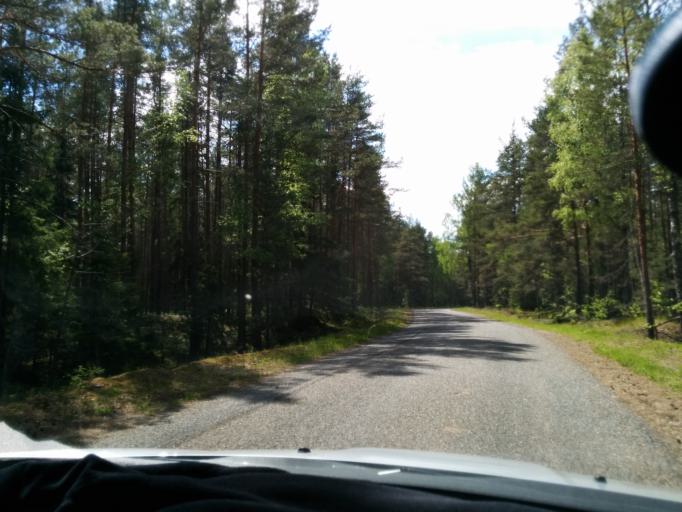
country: EE
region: Harju
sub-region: Loksa linn
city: Loksa
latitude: 59.5498
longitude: 25.9490
